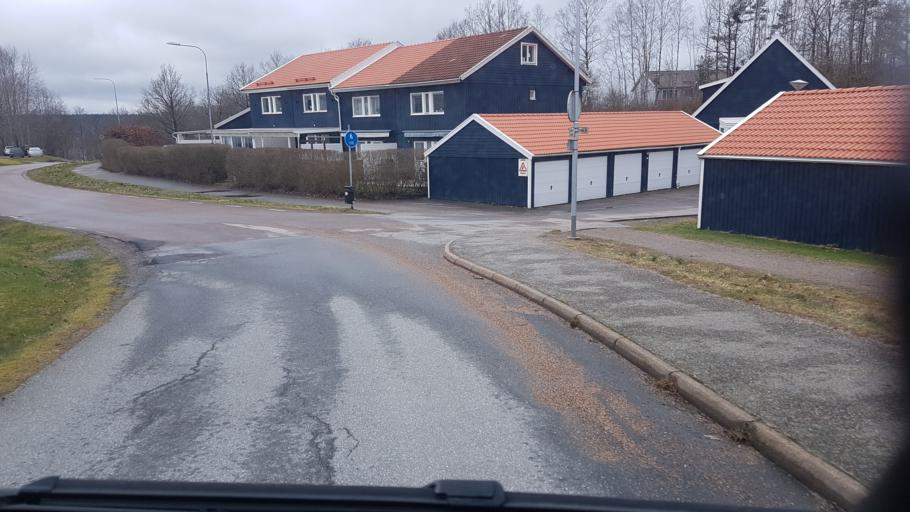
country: SE
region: Vaestra Goetaland
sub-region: Lerums Kommun
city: Lerum
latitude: 57.7551
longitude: 12.2636
